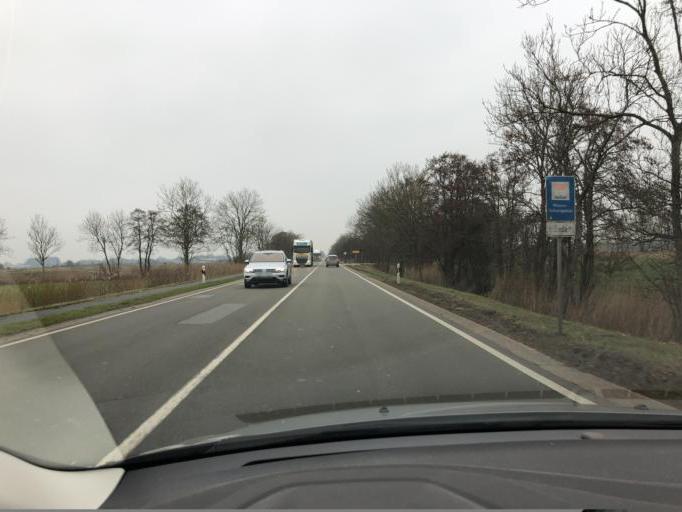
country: DE
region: Lower Saxony
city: Upgant-Schott
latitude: 53.5023
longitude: 7.2975
